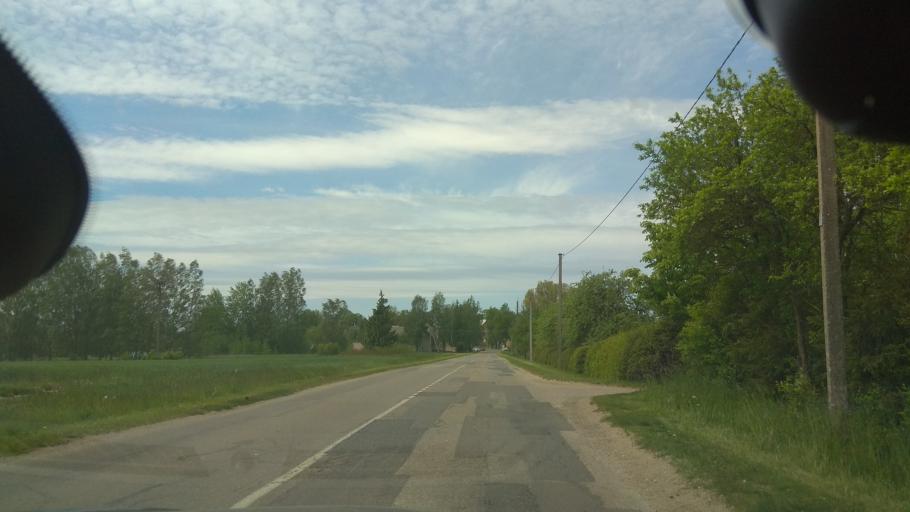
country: LT
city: Sirvintos
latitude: 55.0701
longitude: 24.7770
